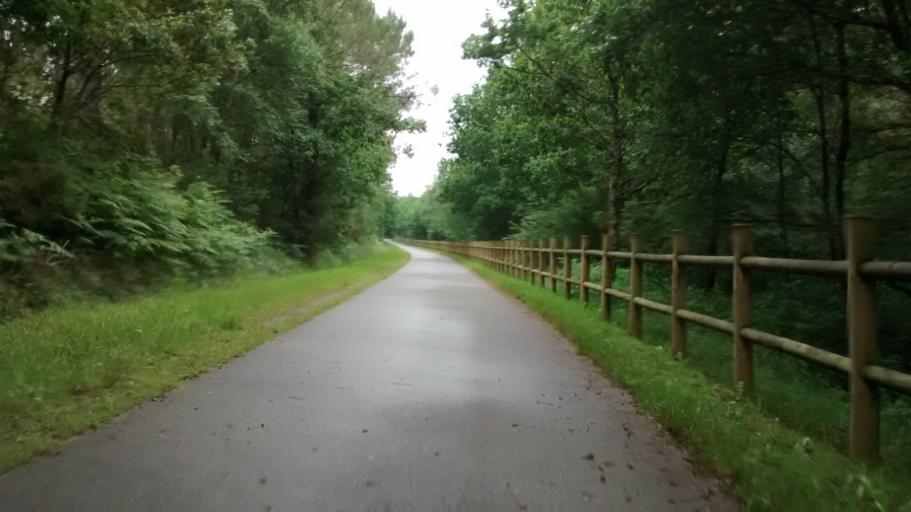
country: FR
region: Brittany
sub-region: Departement du Morbihan
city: Pleucadeuc
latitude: 47.7571
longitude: -2.4008
